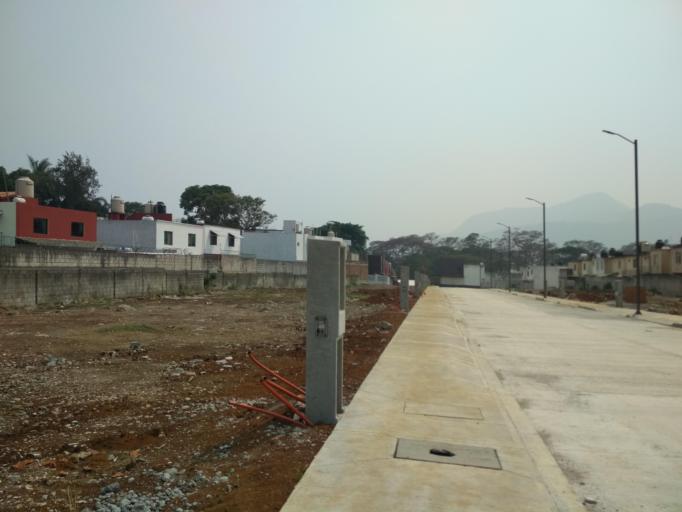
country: MX
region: Veracruz
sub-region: Cordoba
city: Fredepo
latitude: 18.8790
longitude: -96.9677
